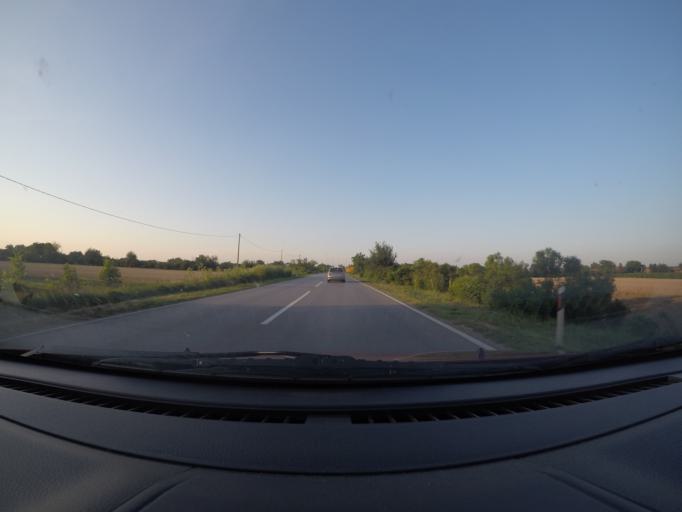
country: RS
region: Central Serbia
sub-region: Branicevski Okrug
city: Pozarevac
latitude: 44.6419
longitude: 21.1549
